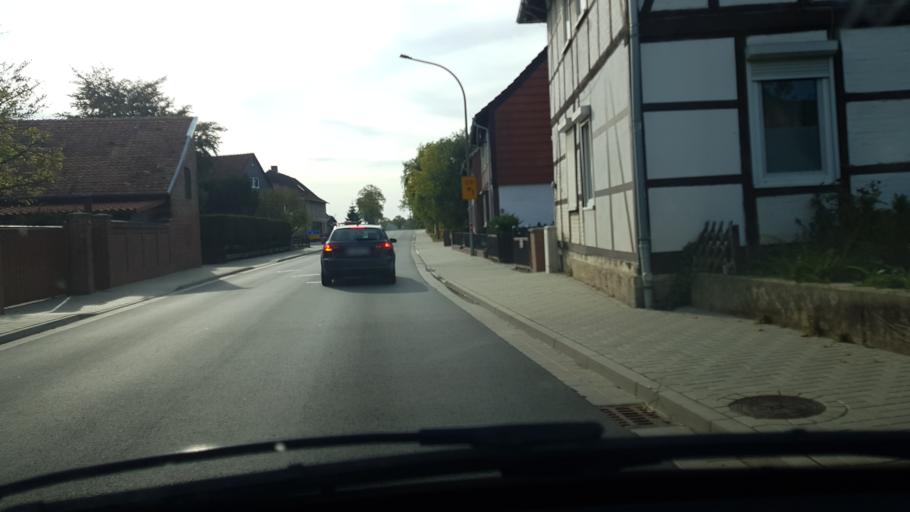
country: DE
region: Lower Saxony
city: Cremlingen
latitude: 52.2918
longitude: 10.6528
